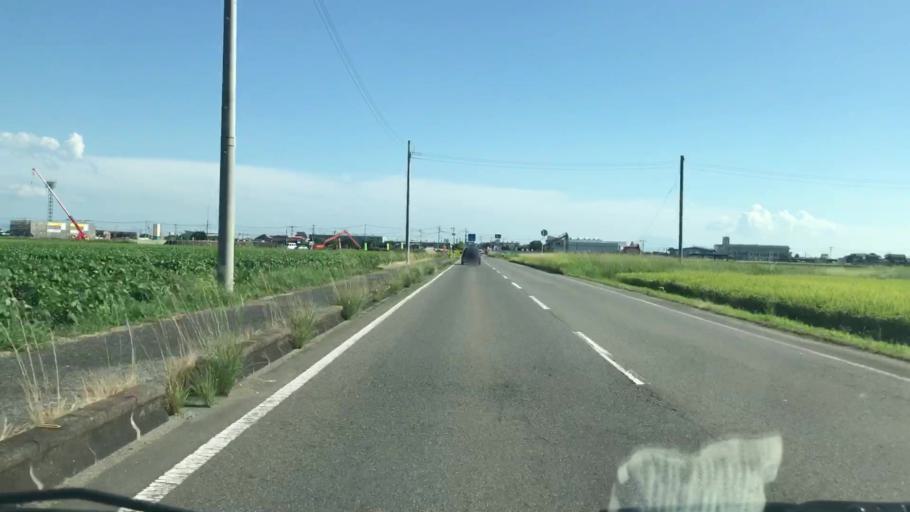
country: JP
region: Saga Prefecture
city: Okawa
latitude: 33.2168
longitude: 130.3348
